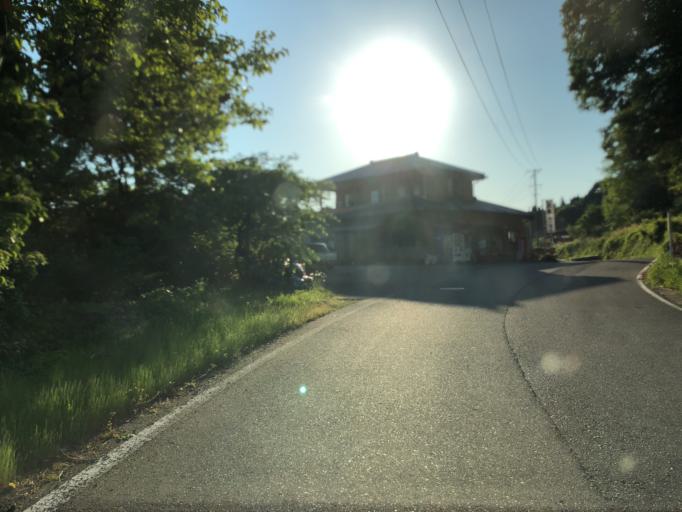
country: JP
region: Fukushima
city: Ishikawa
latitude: 37.0449
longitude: 140.4318
